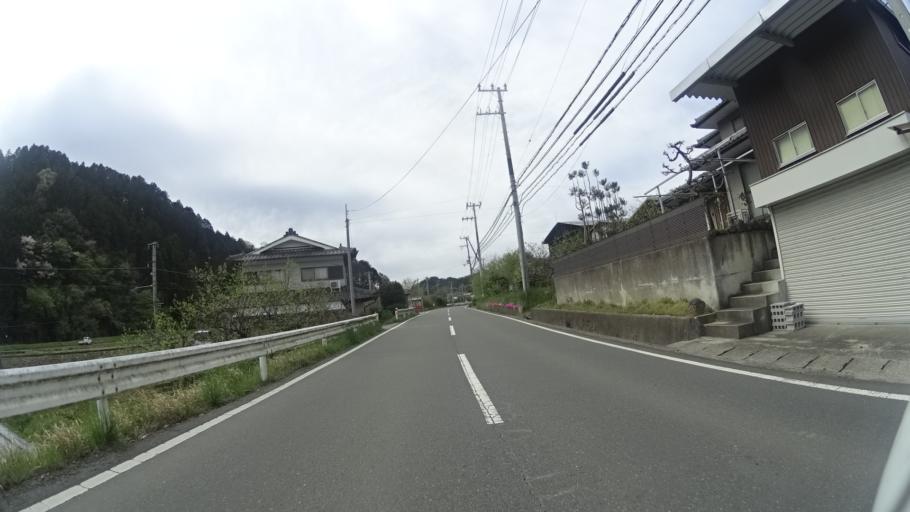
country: JP
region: Kyoto
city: Kameoka
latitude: 35.1912
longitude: 135.4807
